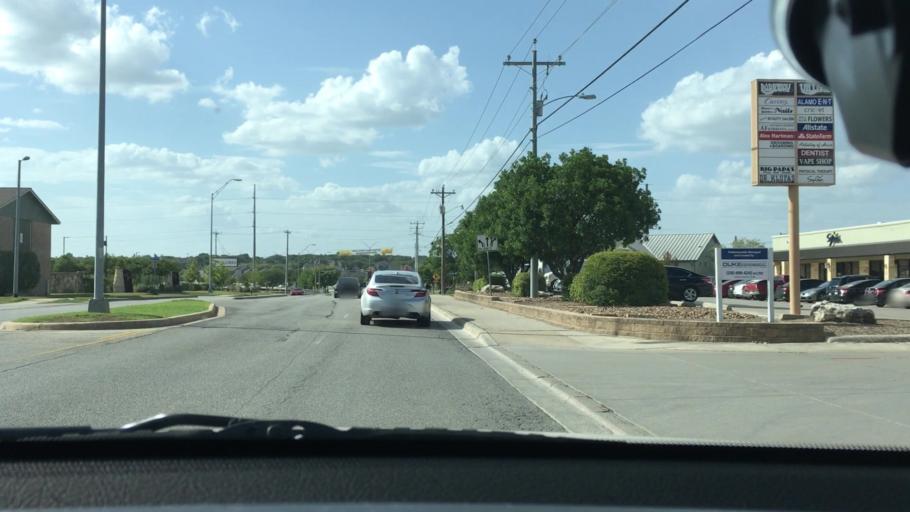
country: US
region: Texas
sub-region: Guadalupe County
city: Schertz
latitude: 29.5666
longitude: -98.2711
